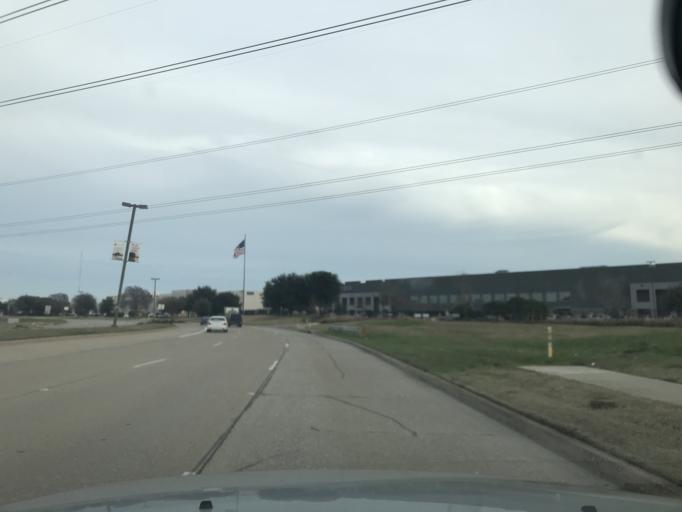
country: US
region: Texas
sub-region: Dallas County
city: Carrollton
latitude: 32.9939
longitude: -96.9334
